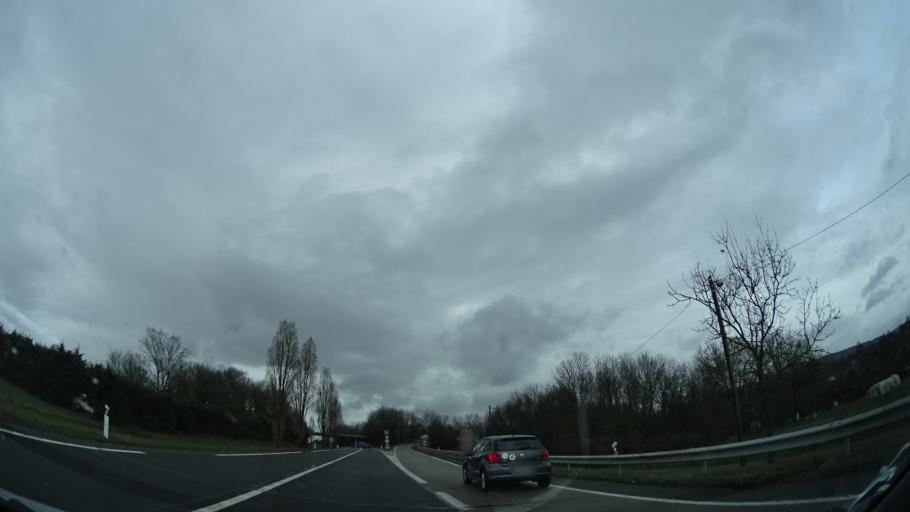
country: FR
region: Rhone-Alpes
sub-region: Departement du Rhone
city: Dardilly
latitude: 45.8077
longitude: 4.7357
